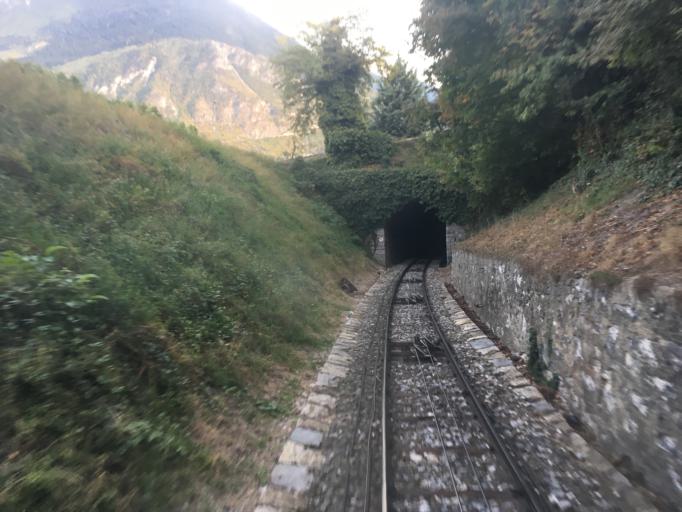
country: CH
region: Valais
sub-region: Sierre District
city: Sierre
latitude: 46.2951
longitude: 7.5291
